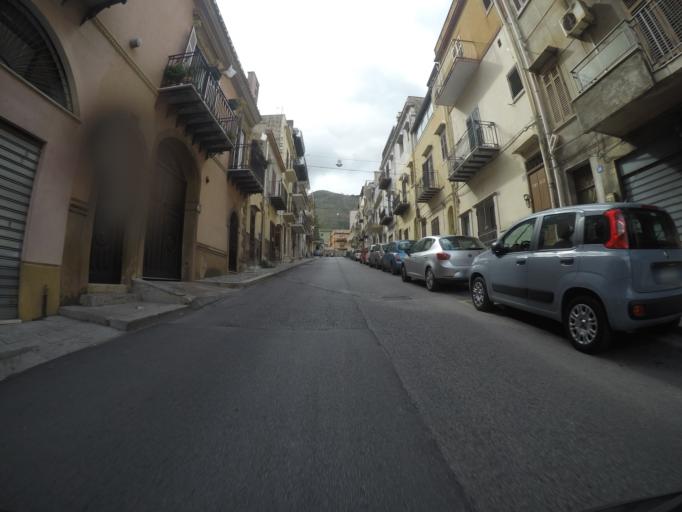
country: IT
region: Sicily
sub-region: Palermo
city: Carini
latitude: 38.1297
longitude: 13.1818
